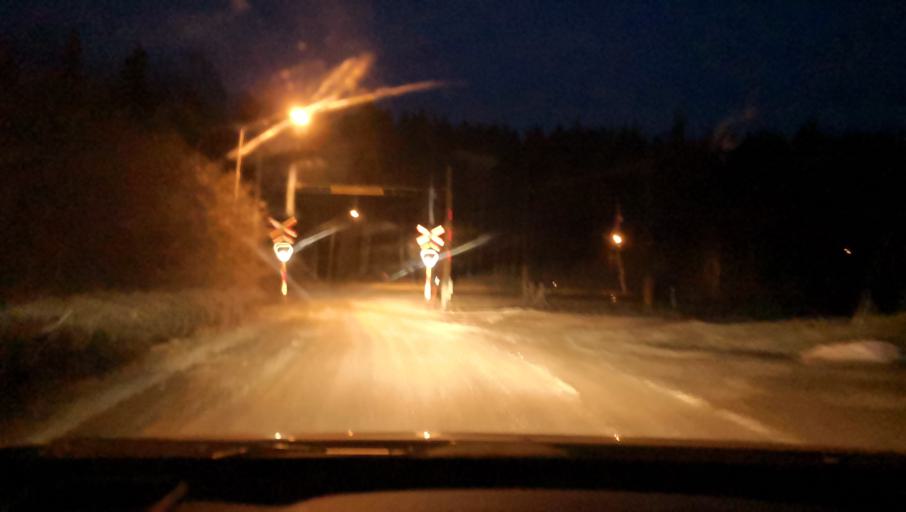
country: SE
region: Vaestmanland
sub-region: Skinnskattebergs Kommun
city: Skinnskatteberg
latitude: 59.6666
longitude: 15.5265
